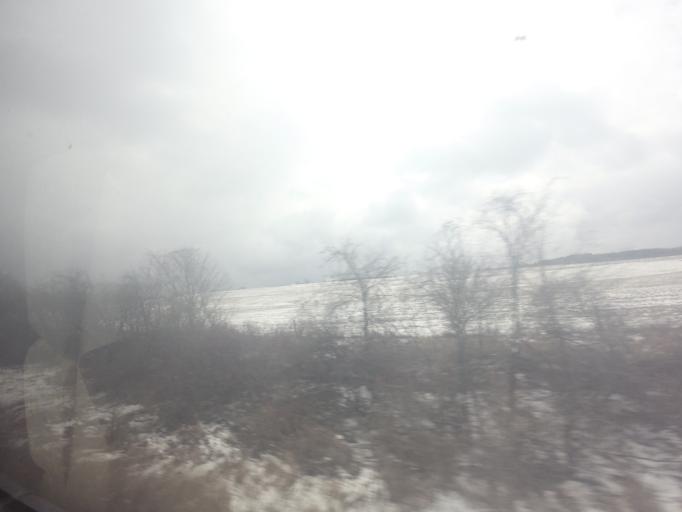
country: CA
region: Ontario
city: Cobourg
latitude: 43.9476
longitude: -78.3660
